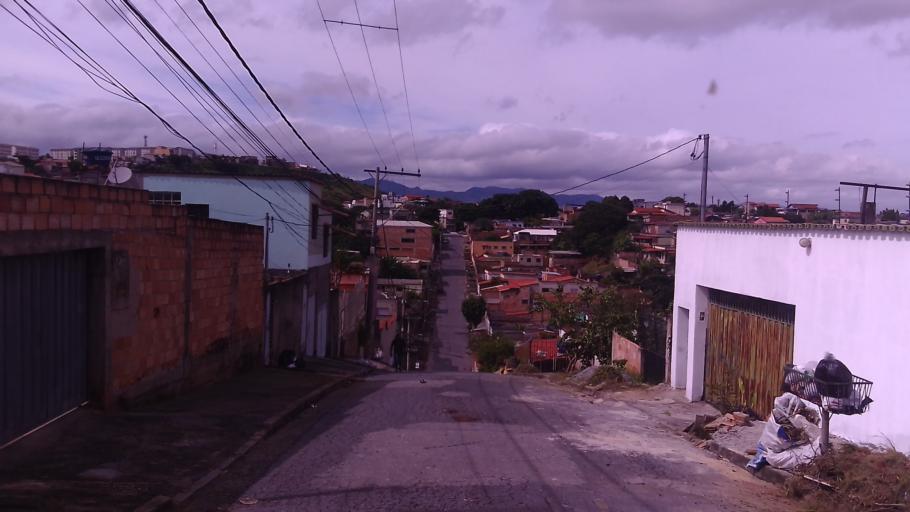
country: BR
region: Minas Gerais
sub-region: Santa Luzia
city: Santa Luzia
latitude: -19.8378
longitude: -43.8939
